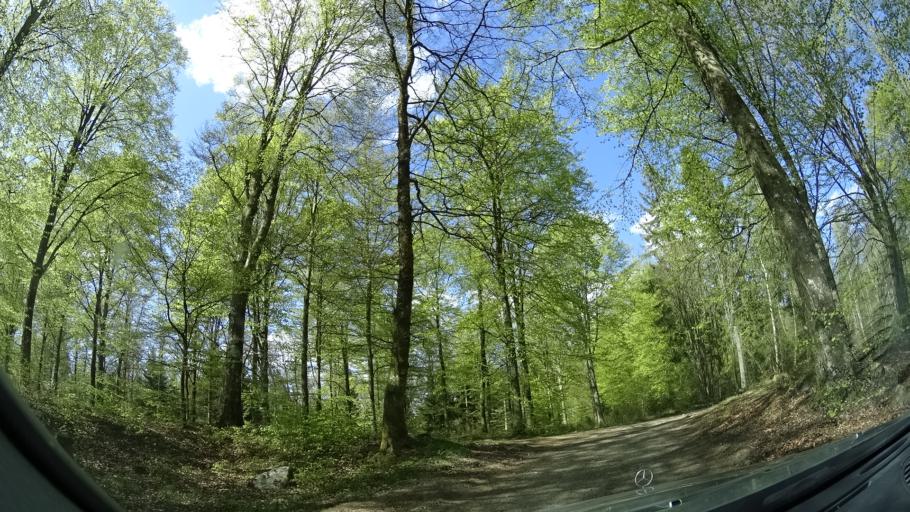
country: SE
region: Skane
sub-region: Hassleholms Kommun
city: Tormestorp
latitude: 56.0972
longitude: 13.6934
